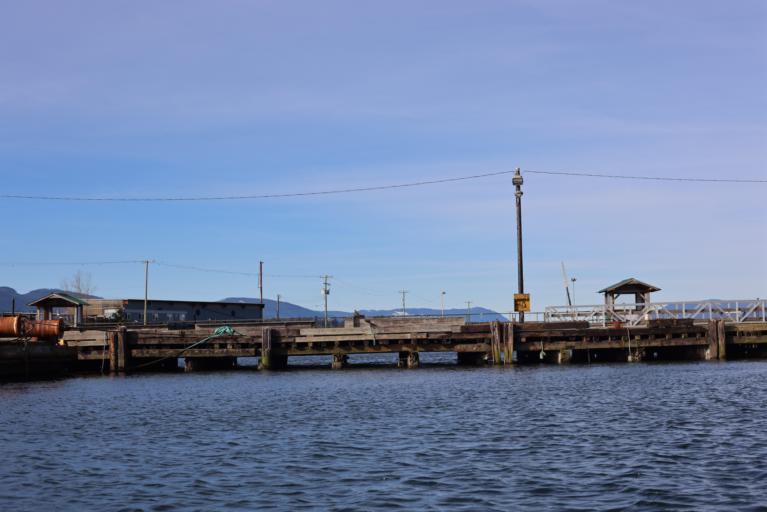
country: CA
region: British Columbia
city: Duncan
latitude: 48.7494
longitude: -123.6230
